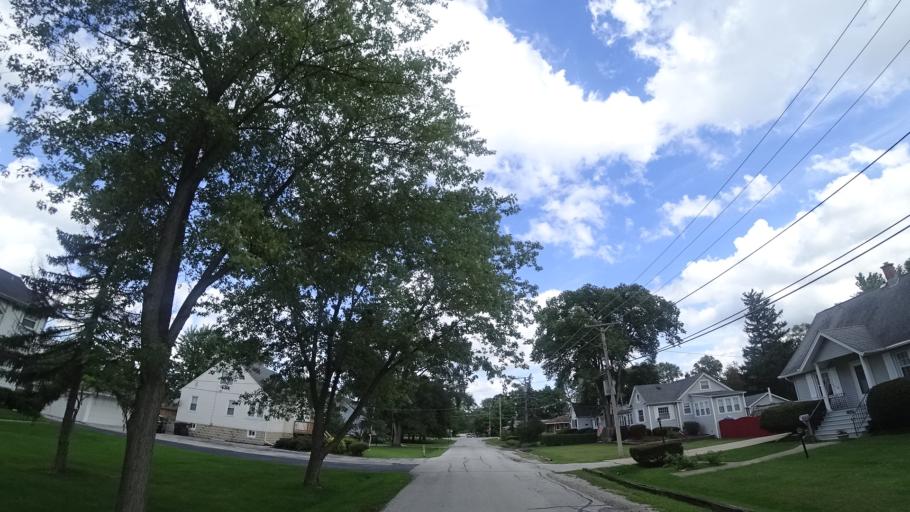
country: US
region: Illinois
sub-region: Cook County
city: Tinley Park
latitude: 41.5724
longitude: -87.7770
